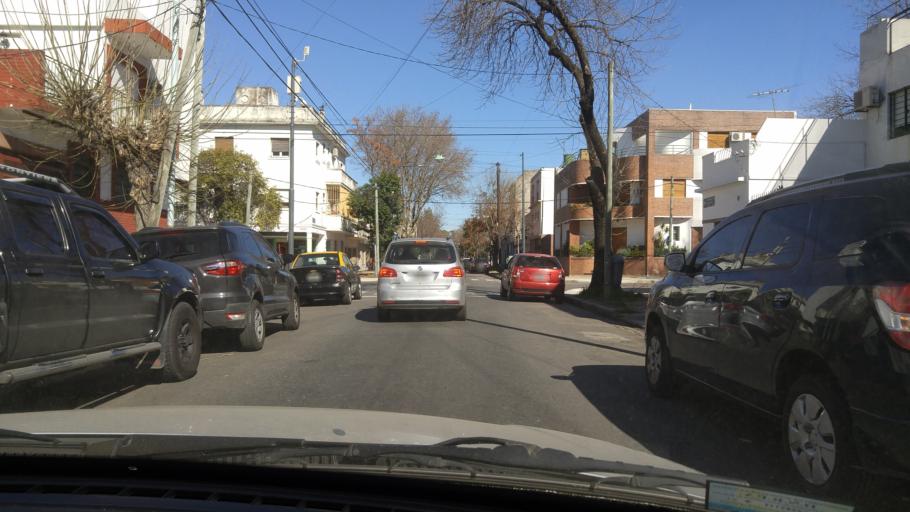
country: AR
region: Buenos Aires F.D.
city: Villa Santa Rita
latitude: -34.6321
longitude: -58.5068
